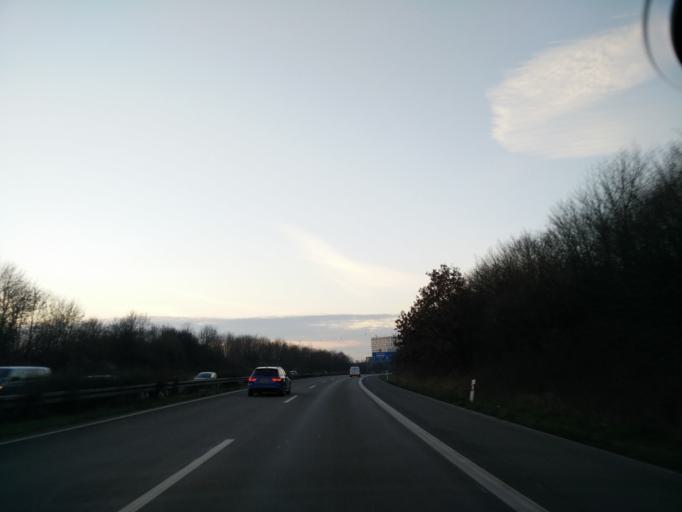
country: DE
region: North Rhine-Westphalia
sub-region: Regierungsbezirk Dusseldorf
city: Ratingen
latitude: 51.2746
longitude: 6.8184
